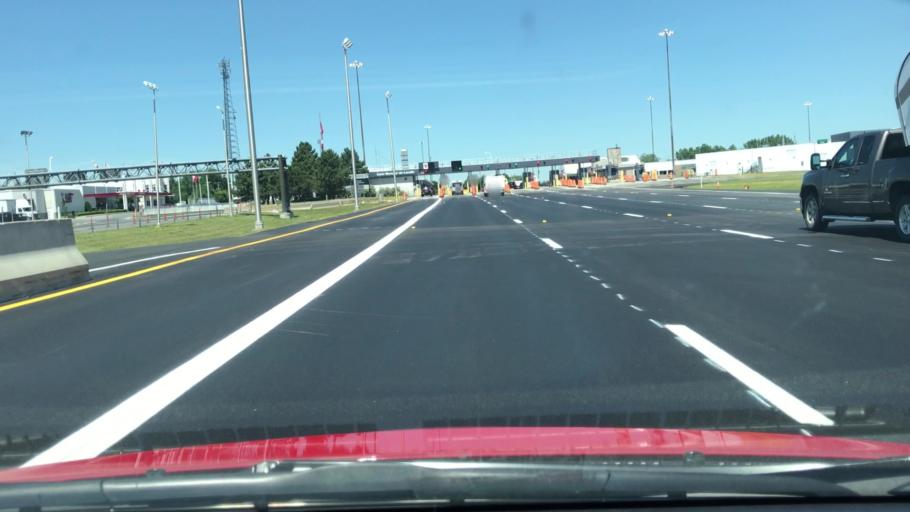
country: US
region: New York
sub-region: Clinton County
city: Champlain
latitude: 45.0078
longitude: -73.4520
